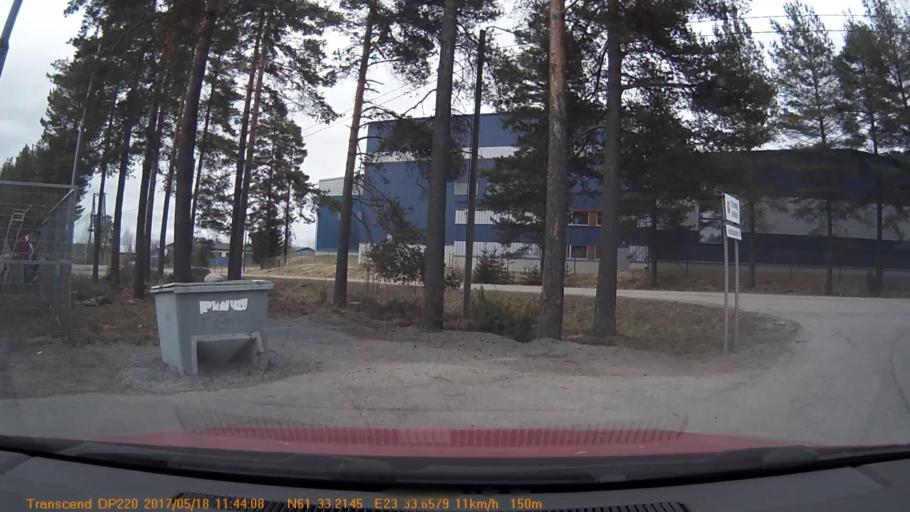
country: FI
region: Pirkanmaa
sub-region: Tampere
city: Yloejaervi
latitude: 61.5536
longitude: 23.5610
